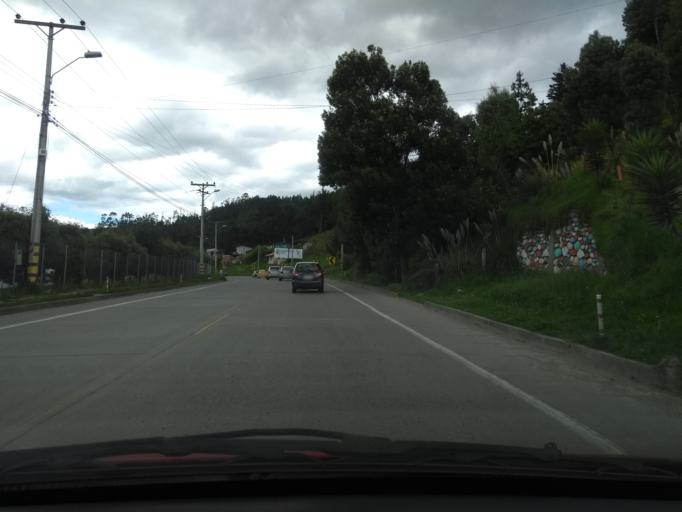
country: EC
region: Azuay
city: Cuenca
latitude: -2.9937
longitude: -79.0458
